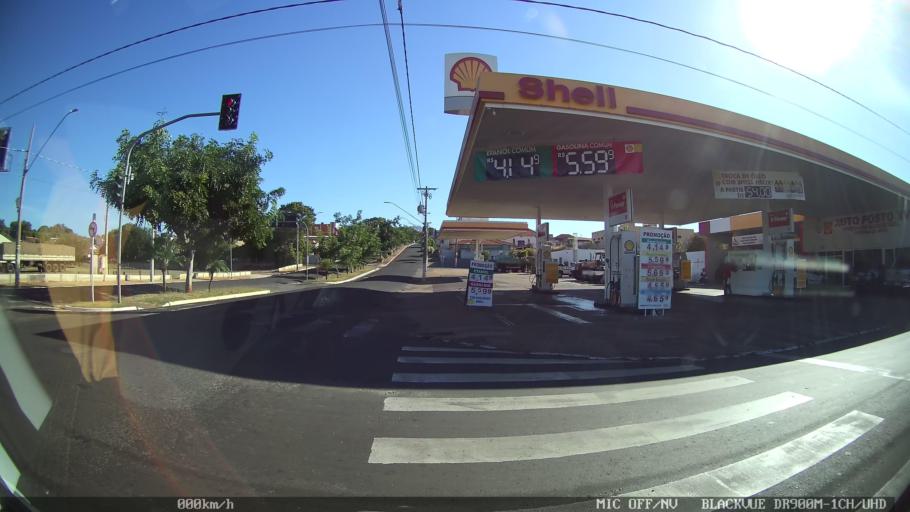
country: BR
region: Sao Paulo
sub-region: Olimpia
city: Olimpia
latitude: -20.7404
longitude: -48.9103
